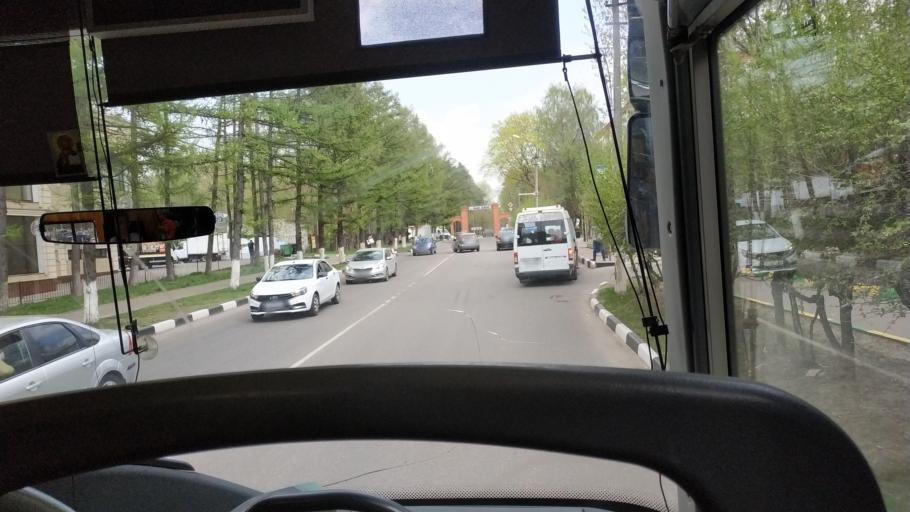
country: RU
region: Moskovskaya
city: Lytkarino
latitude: 55.5782
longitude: 37.9097
